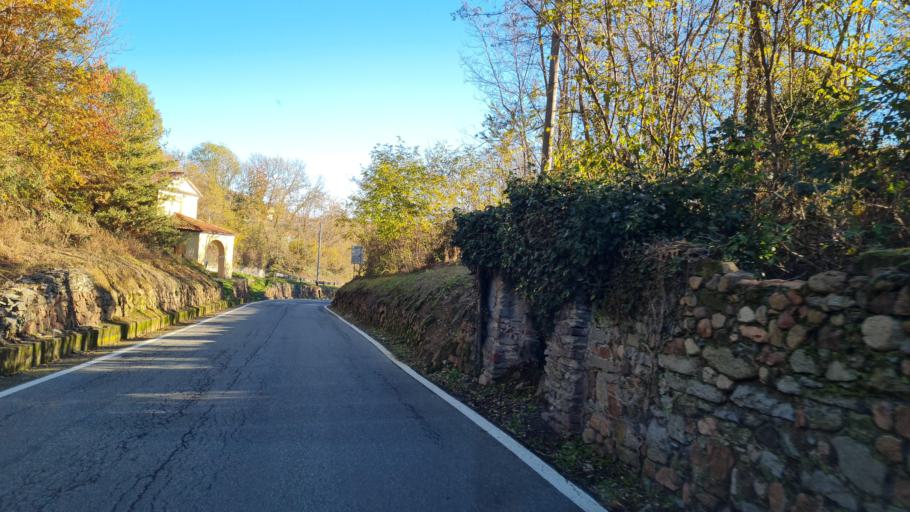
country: IT
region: Piedmont
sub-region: Provincia di Biella
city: Brusnengo
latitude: 45.5942
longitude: 8.2415
